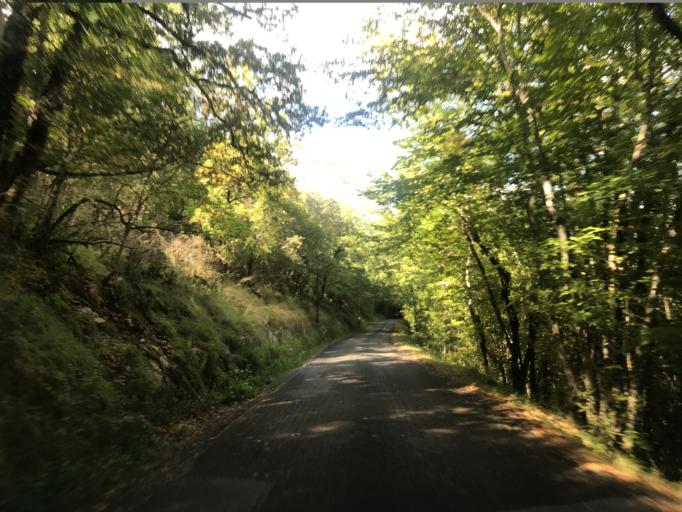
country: FR
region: Aquitaine
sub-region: Departement de la Dordogne
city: Rouffignac-Saint-Cernin-de-Reilhac
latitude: 44.9722
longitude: 1.0323
